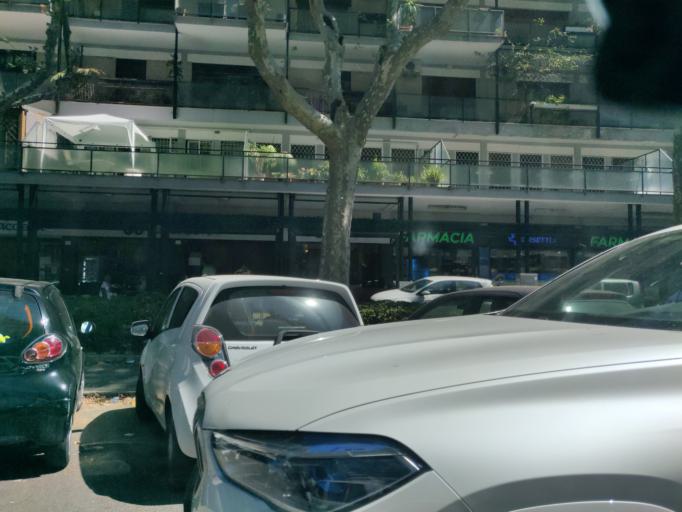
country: IT
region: Latium
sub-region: Citta metropolitana di Roma Capitale
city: Selcetta
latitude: 41.8263
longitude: 12.4750
